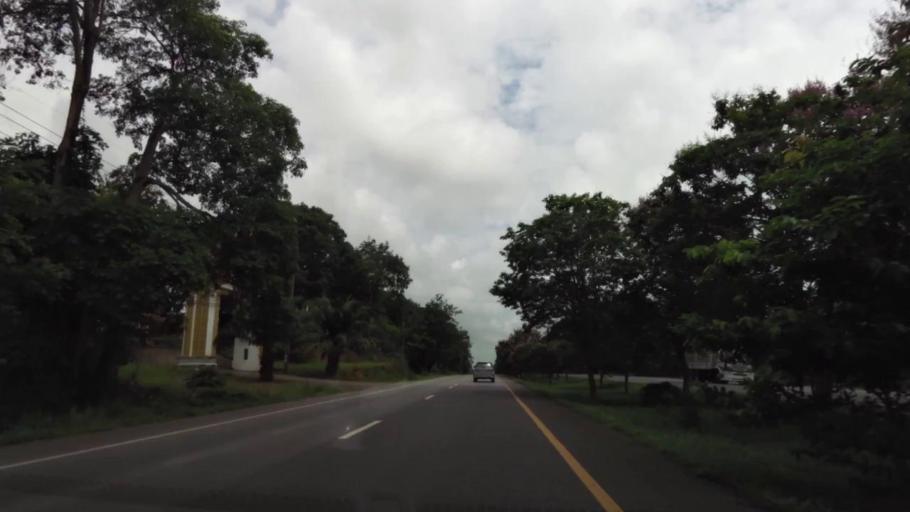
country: TH
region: Chanthaburi
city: Na Yai Am
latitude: 12.7454
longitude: 101.8831
